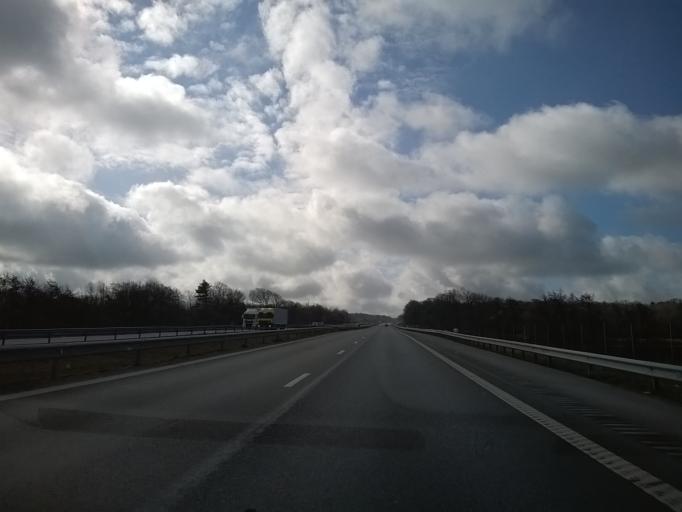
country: SE
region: Halland
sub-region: Kungsbacka Kommun
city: Frillesas
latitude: 57.2986
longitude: 12.2151
